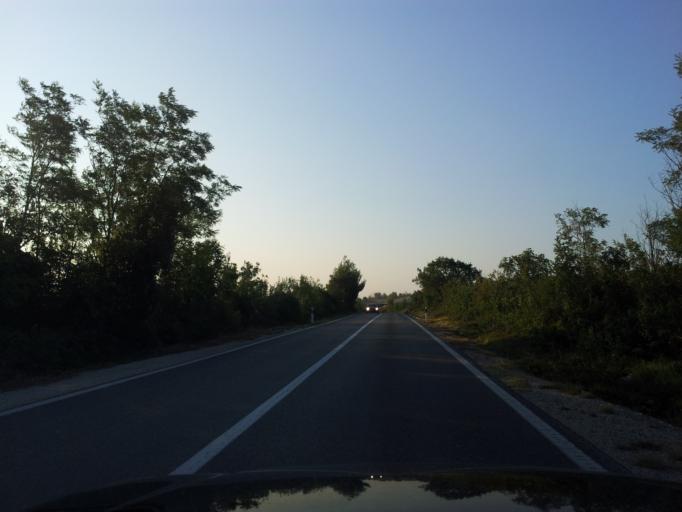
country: HR
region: Zadarska
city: Polaca
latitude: 44.0163
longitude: 15.5402
